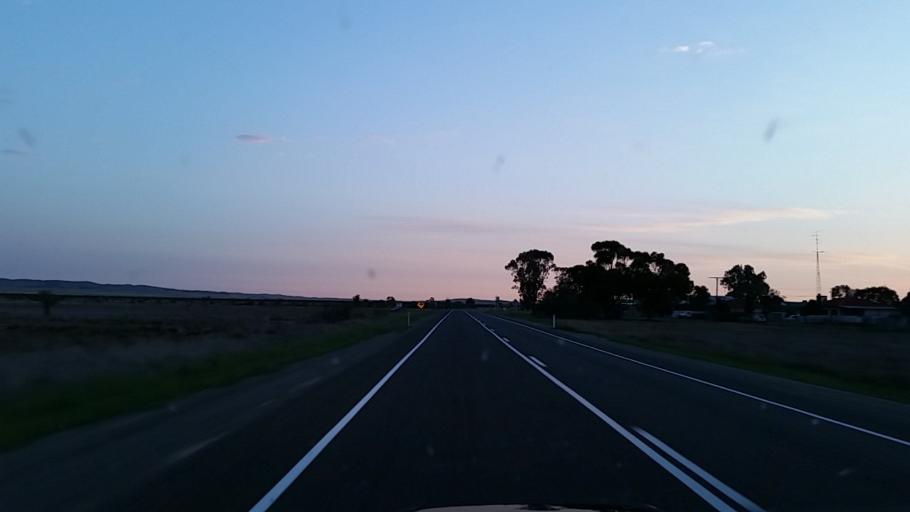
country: AU
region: South Australia
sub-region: Peterborough
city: Peterborough
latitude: -33.1515
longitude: 138.9238
